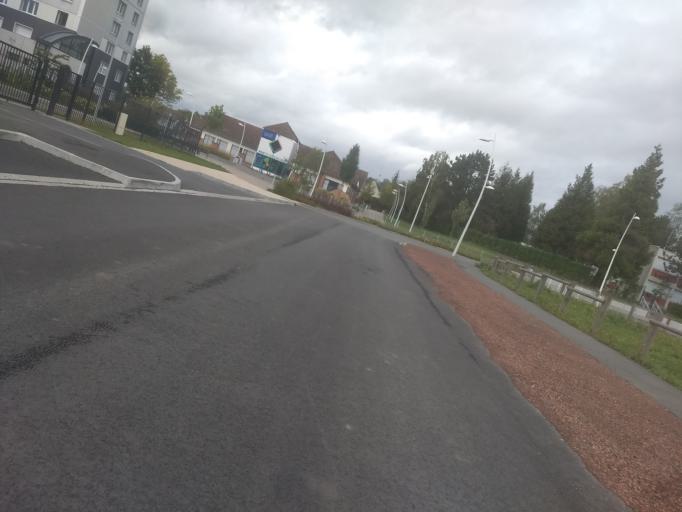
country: FR
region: Nord-Pas-de-Calais
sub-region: Departement du Pas-de-Calais
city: Saint-Nicolas
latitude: 50.3055
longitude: 2.7936
